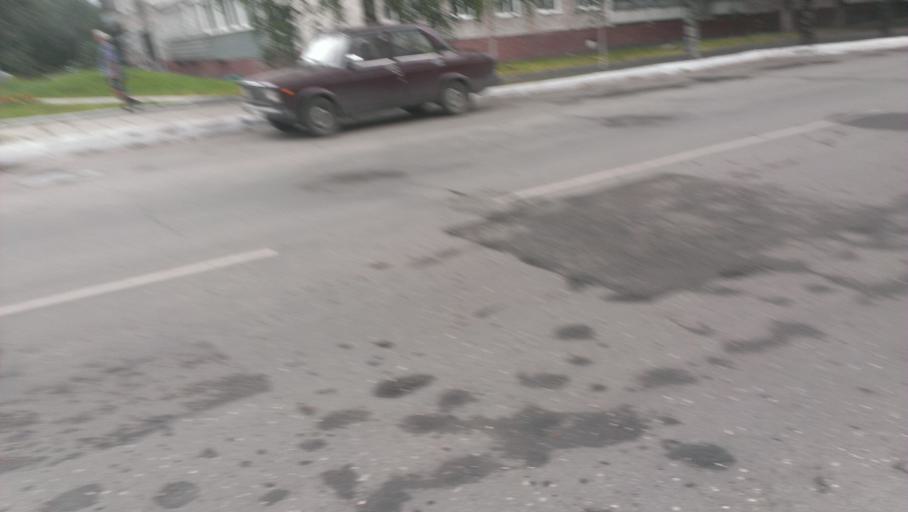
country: RU
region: Altai Krai
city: Novosilikatnyy
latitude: 53.3727
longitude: 83.6698
